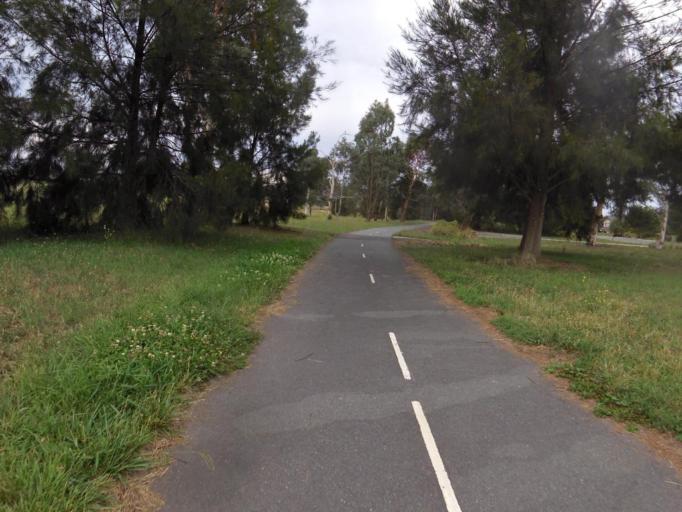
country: AU
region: Australian Capital Territory
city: Kaleen
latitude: -35.1670
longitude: 149.1412
